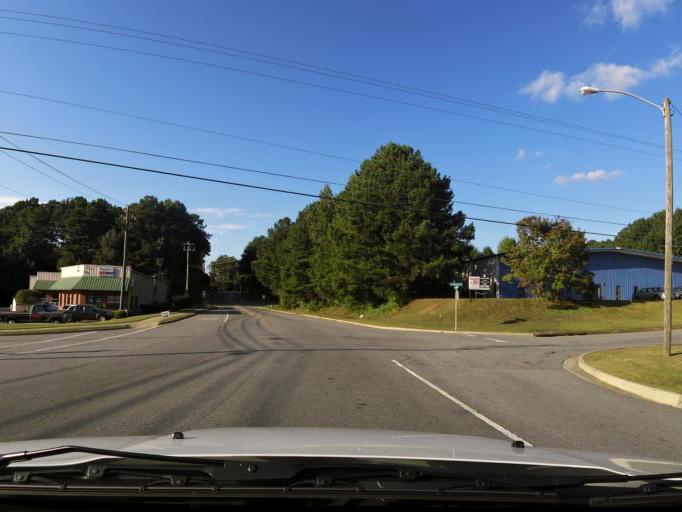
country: US
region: Georgia
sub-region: Cobb County
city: Kennesaw
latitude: 34.0327
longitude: -84.6163
